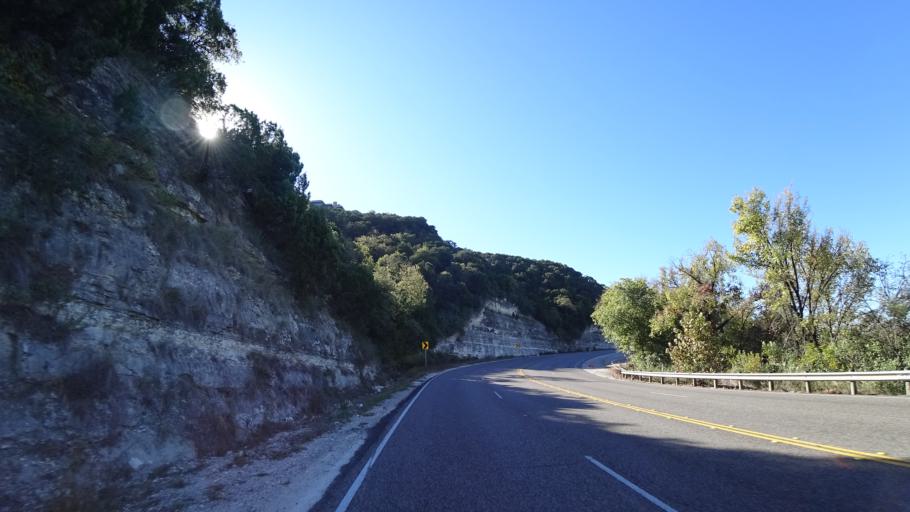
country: US
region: Texas
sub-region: Travis County
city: West Lake Hills
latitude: 30.3540
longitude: -97.7823
